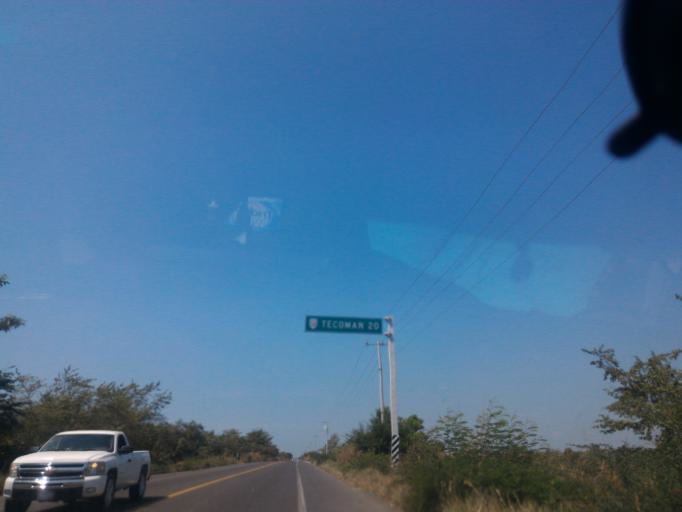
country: MX
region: Michoacan
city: Coahuayana Viejo
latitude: 18.7737
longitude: -103.7451
